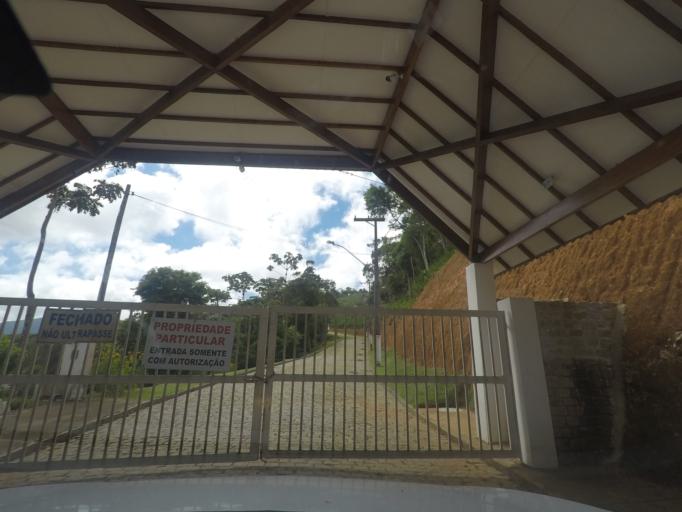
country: BR
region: Rio de Janeiro
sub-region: Teresopolis
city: Teresopolis
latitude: -22.4053
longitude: -42.9836
